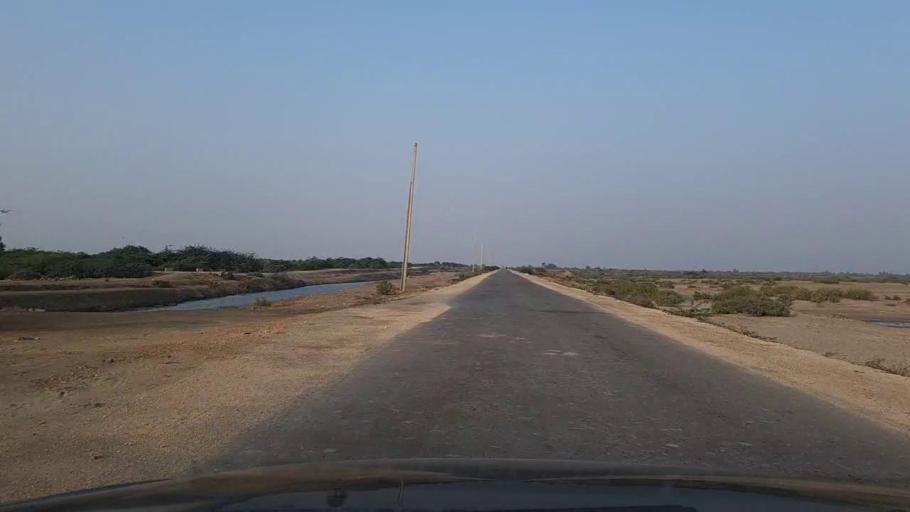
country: PK
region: Sindh
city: Mirpur Sakro
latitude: 24.4695
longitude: 67.7996
